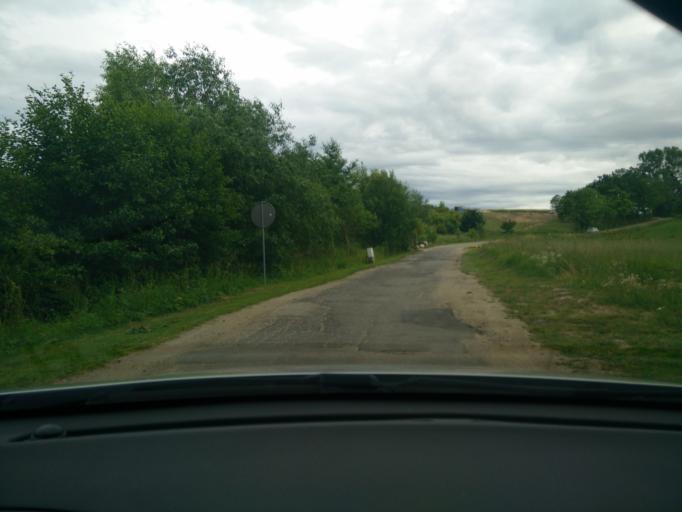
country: PL
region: Pomeranian Voivodeship
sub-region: Powiat pucki
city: Mrzezino
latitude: 54.6643
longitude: 18.4564
